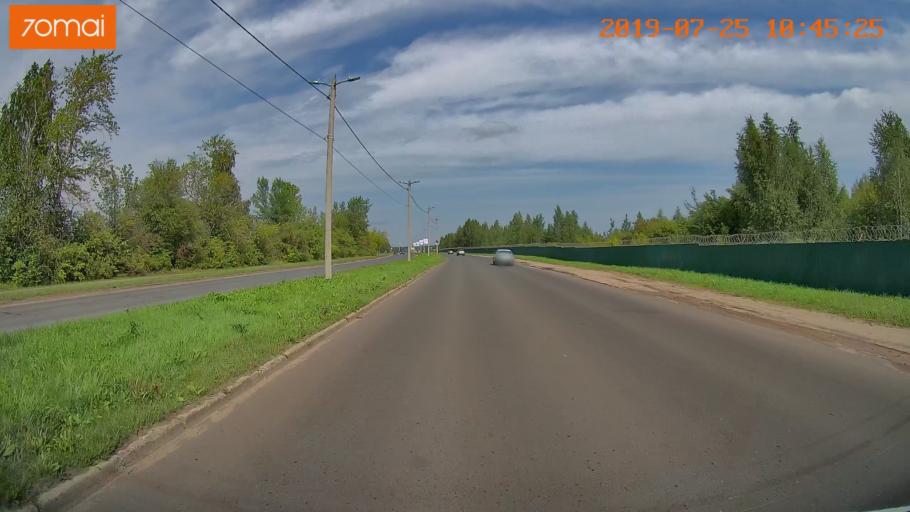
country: RU
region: Ivanovo
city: Bogorodskoye
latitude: 57.0501
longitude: 40.9656
